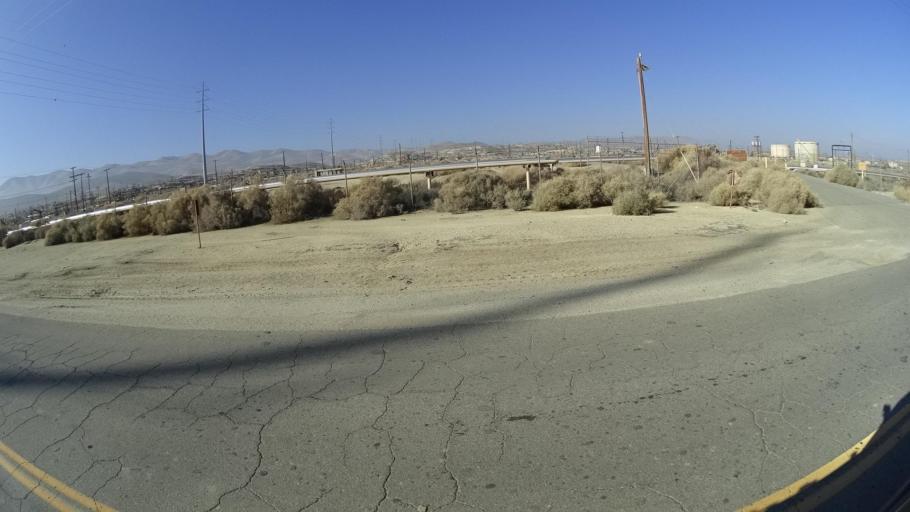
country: US
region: California
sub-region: Kern County
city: Taft Heights
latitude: 35.2100
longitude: -119.5981
